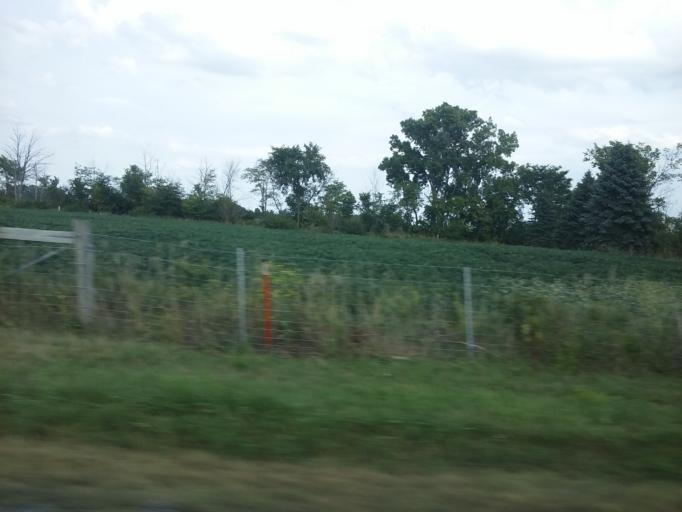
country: US
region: Ohio
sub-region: Wood County
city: Bowling Green
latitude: 41.2900
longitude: -83.6502
